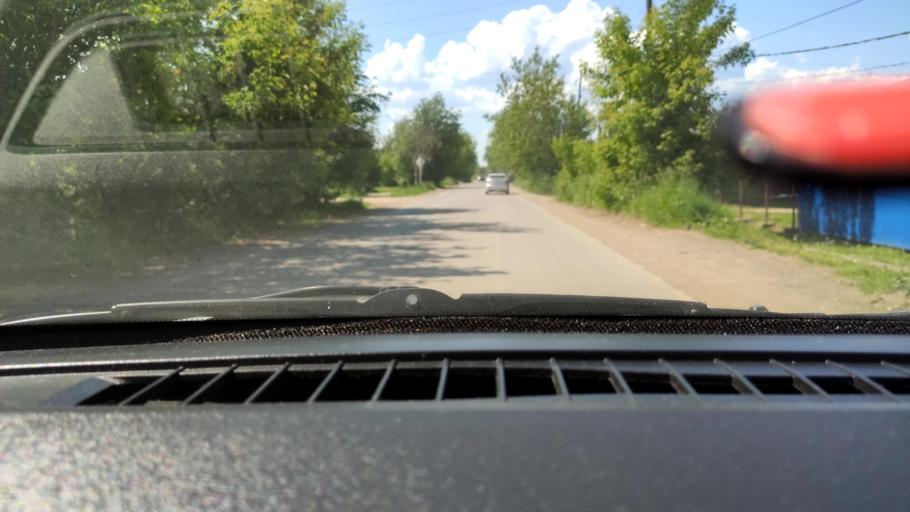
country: RU
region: Perm
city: Sylva
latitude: 58.0327
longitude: 56.7699
